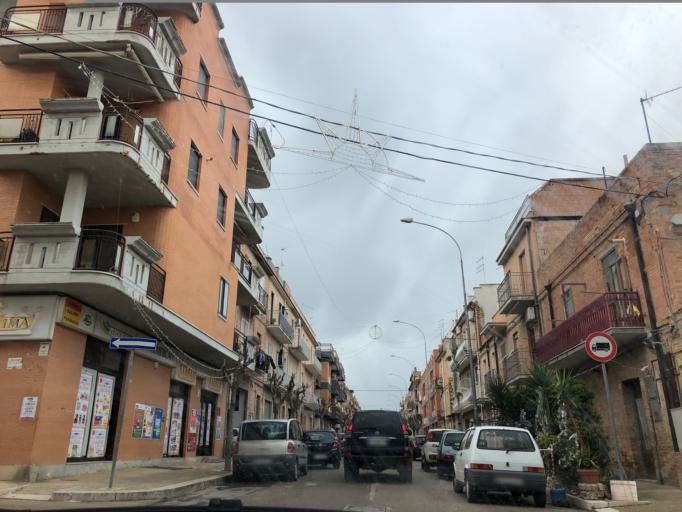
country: IT
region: Apulia
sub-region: Provincia di Foggia
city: Lucera
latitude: 41.5076
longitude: 15.3273
